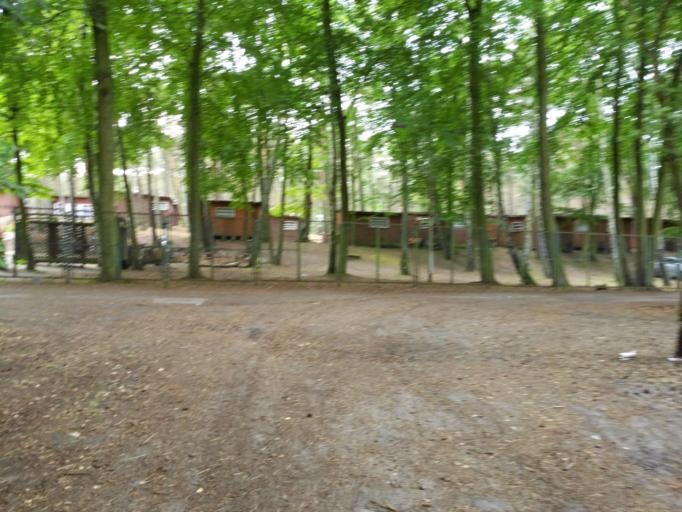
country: PL
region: Pomeranian Voivodeship
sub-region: Gdansk
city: Gdansk
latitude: 54.3693
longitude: 18.7320
